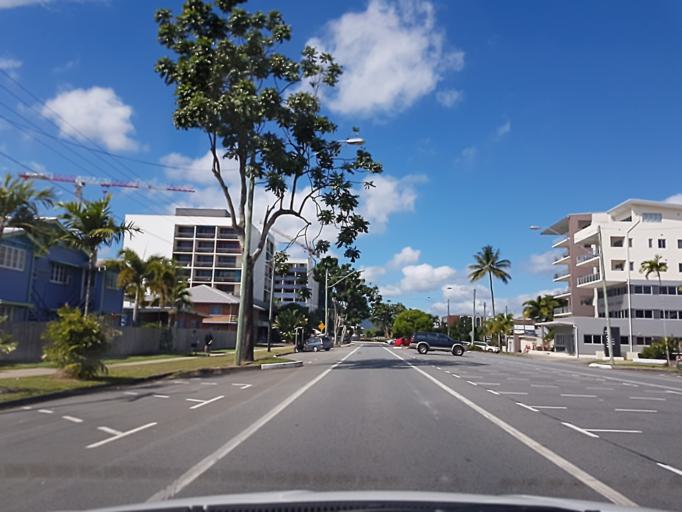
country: AU
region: Queensland
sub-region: Cairns
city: Cairns
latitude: -16.9150
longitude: 145.7716
